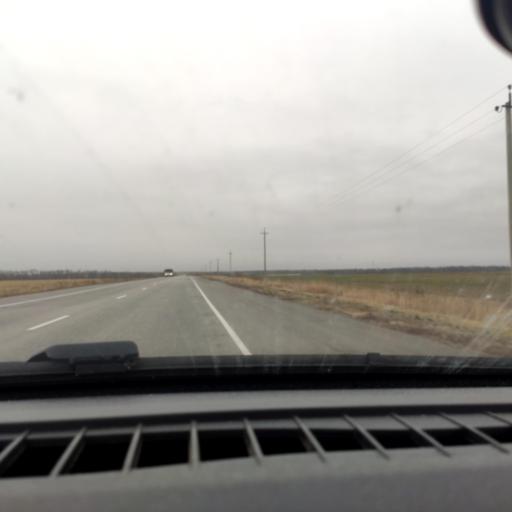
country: RU
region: Voronezj
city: Devitsa
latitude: 51.5624
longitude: 38.9735
